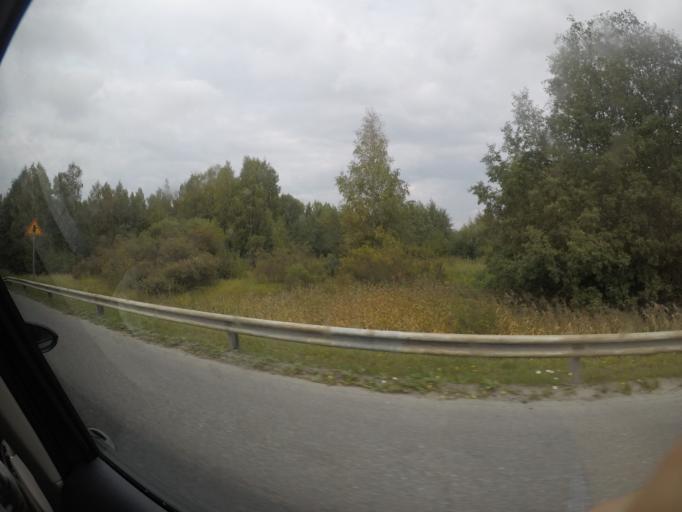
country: FI
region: Haeme
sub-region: Haemeenlinna
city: Parola
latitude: 61.0412
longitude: 24.4019
